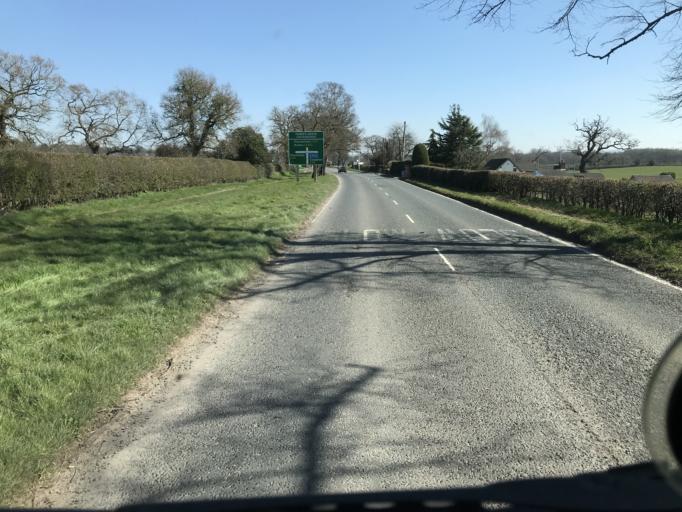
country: GB
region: England
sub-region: Cheshire East
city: Siddington
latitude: 53.2642
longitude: -2.2393
